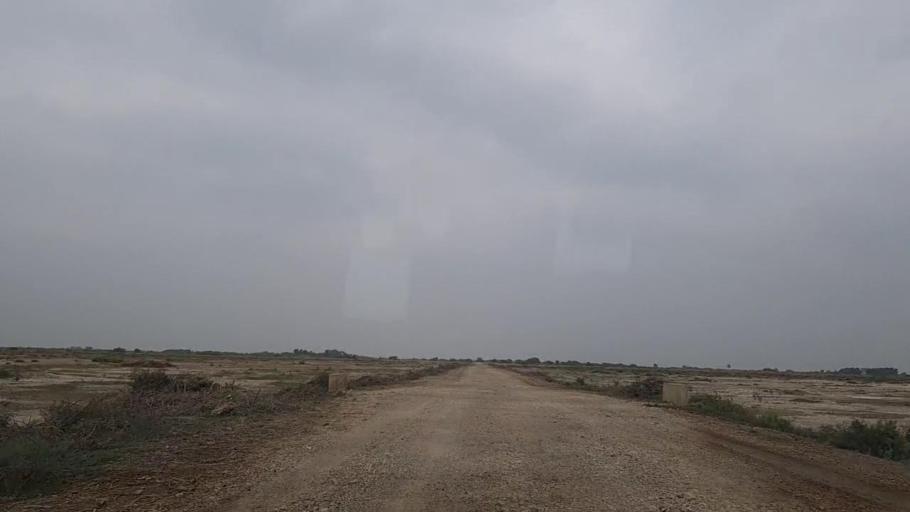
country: PK
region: Sindh
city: Mirpur Sakro
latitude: 24.6313
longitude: 67.7194
